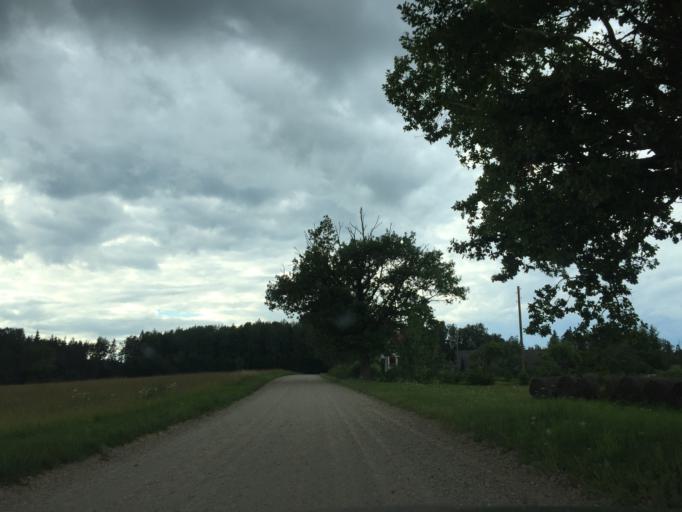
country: LV
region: Malpils
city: Malpils
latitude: 56.9393
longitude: 25.0106
